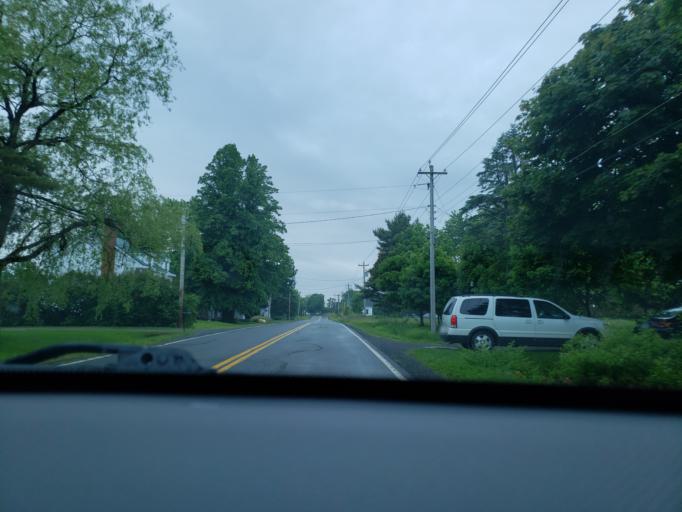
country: CA
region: Nova Scotia
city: Windsor
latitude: 45.0580
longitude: -63.9977
